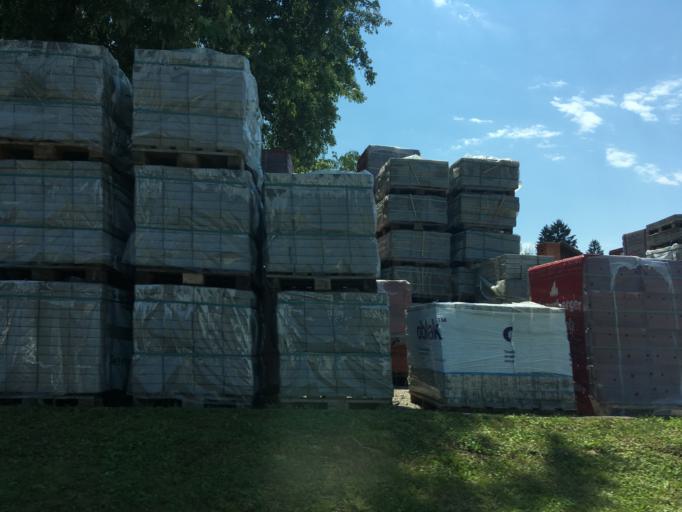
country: SI
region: Metlika
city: Metlika
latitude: 45.6493
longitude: 15.3107
